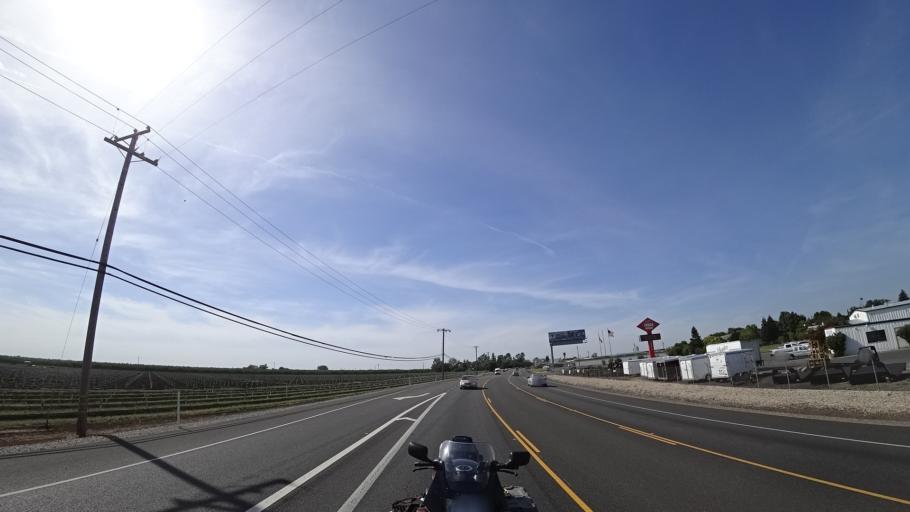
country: US
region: California
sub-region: Butte County
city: Chico
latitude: 39.7939
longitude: -121.8998
